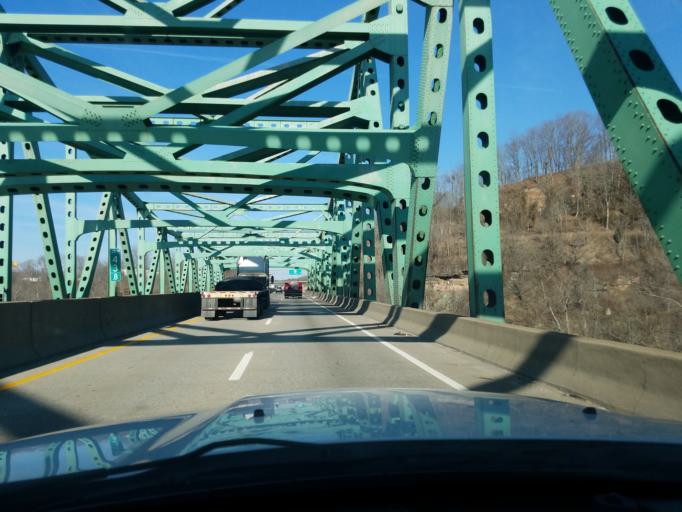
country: US
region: West Virginia
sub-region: Kanawha County
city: Nitro
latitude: 38.4456
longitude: -81.8434
